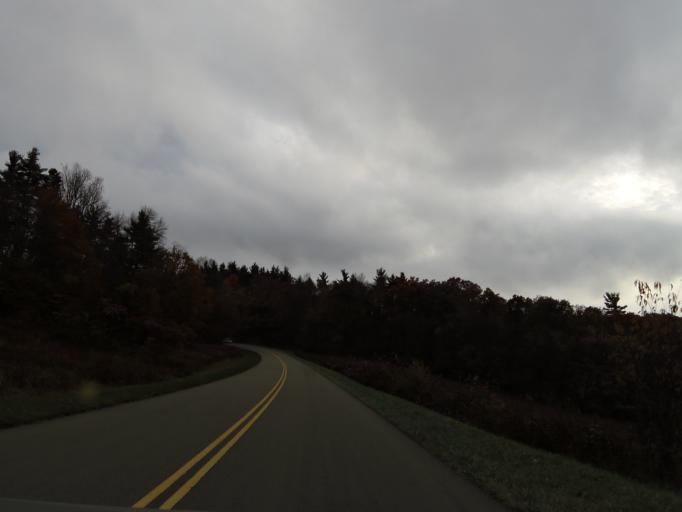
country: US
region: North Carolina
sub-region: Ashe County
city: Jefferson
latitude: 36.3330
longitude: -81.3746
